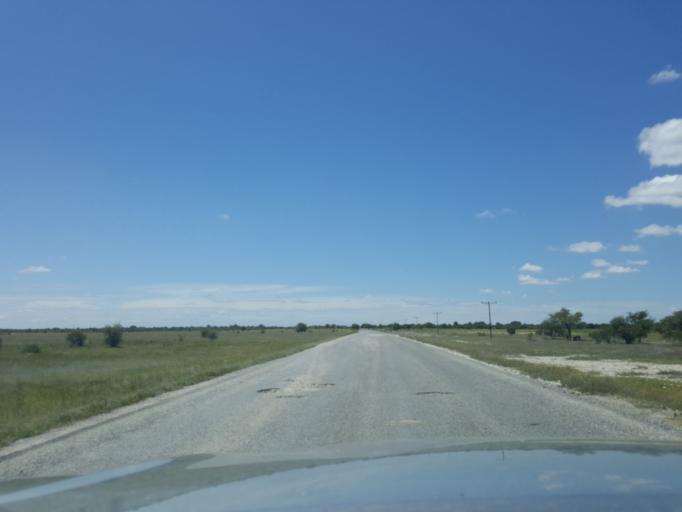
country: BW
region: Central
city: Nata
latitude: -20.1582
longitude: 25.8412
